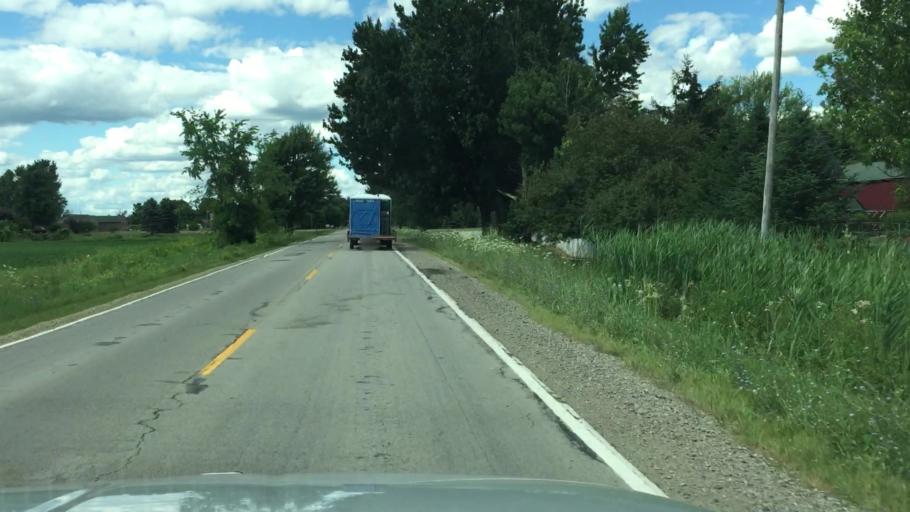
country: US
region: Michigan
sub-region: Macomb County
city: Armada
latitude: 42.9032
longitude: -82.9452
